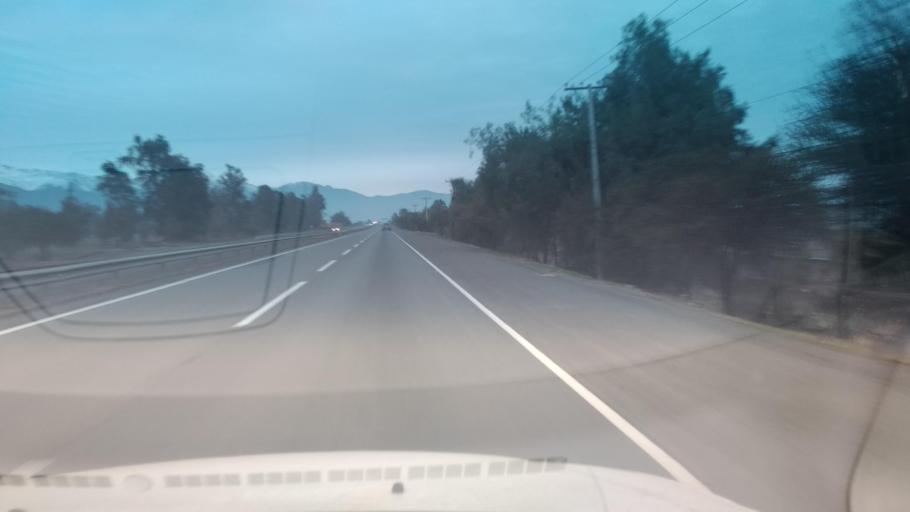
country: CL
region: Santiago Metropolitan
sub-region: Provincia de Chacabuco
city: Chicureo Abajo
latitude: -33.1366
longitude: -70.6658
